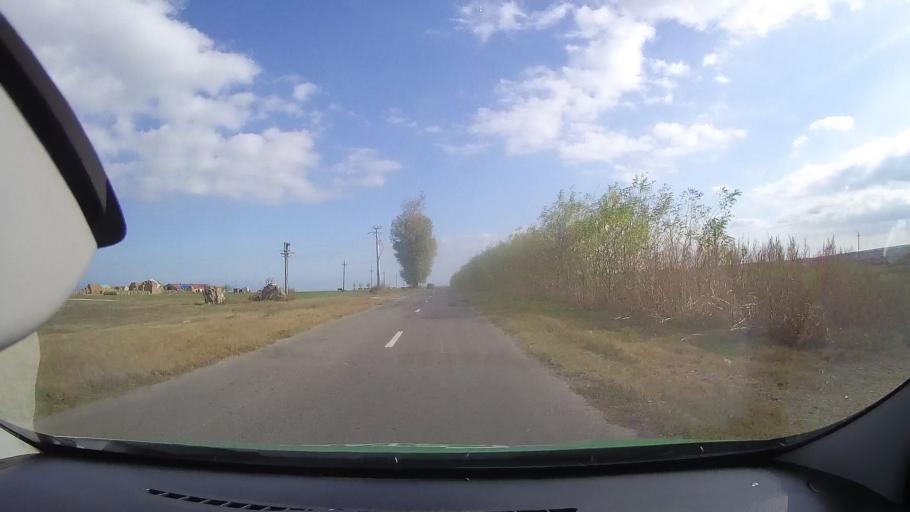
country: RO
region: Constanta
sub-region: Comuna Istria
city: Nuntasi
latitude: 44.5341
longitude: 28.6652
